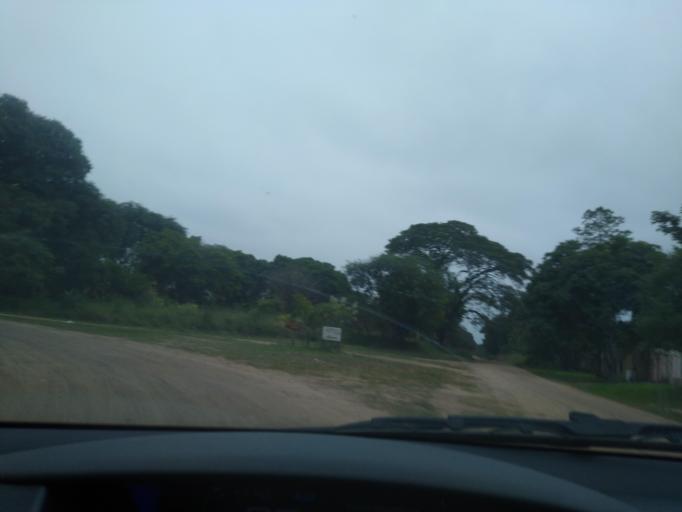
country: AR
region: Chaco
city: Colonia Benitez
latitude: -27.3301
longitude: -58.9638
